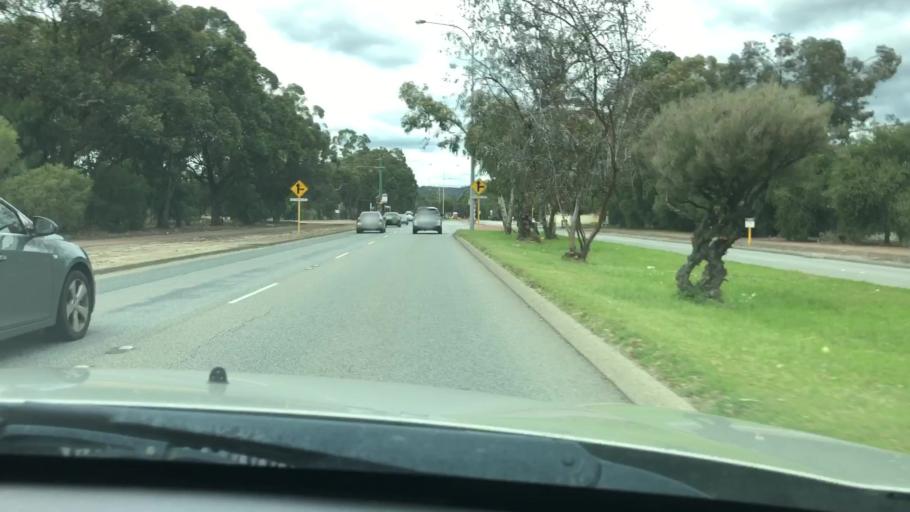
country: AU
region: Western Australia
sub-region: Armadale
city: Seville Grove
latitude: -32.1470
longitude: 115.9941
